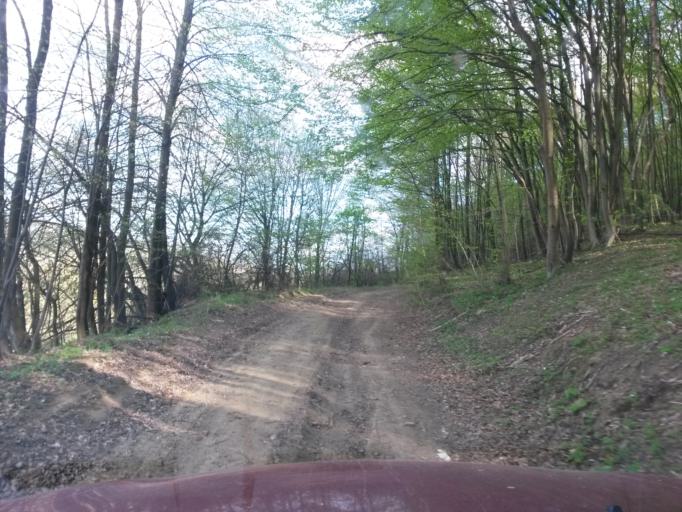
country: SK
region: Presovsky
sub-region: Okres Presov
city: Presov
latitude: 48.9527
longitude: 21.1536
